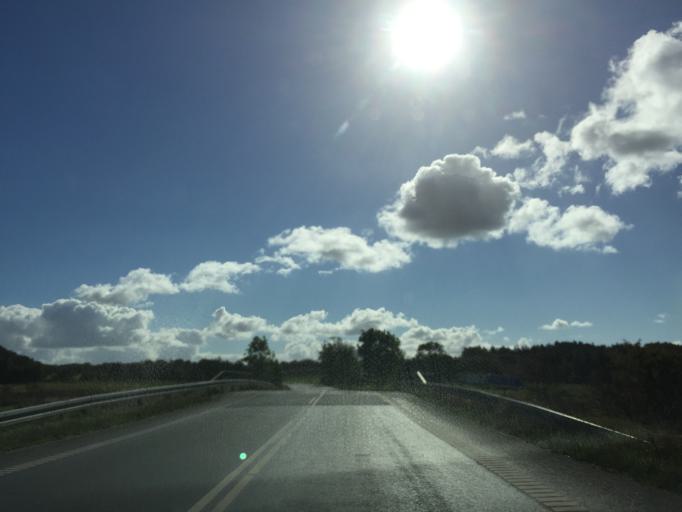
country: DK
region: Central Jutland
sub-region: Viborg Kommune
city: Bjerringbro
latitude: 56.4362
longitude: 9.5512
